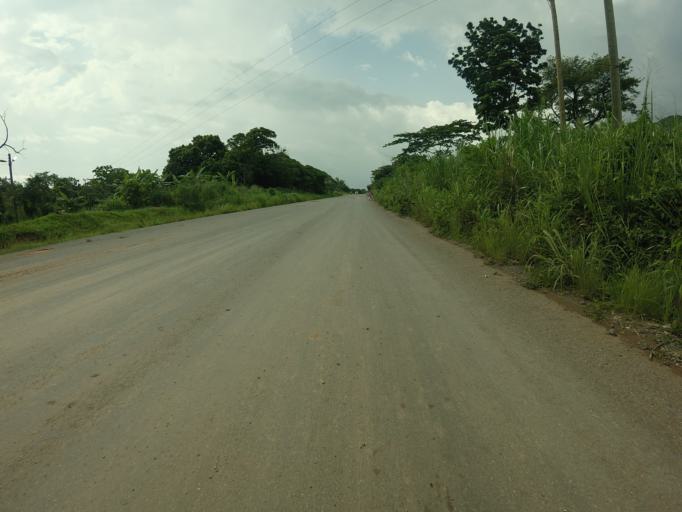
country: GH
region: Volta
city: Kpandu
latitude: 6.8780
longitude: 0.4206
